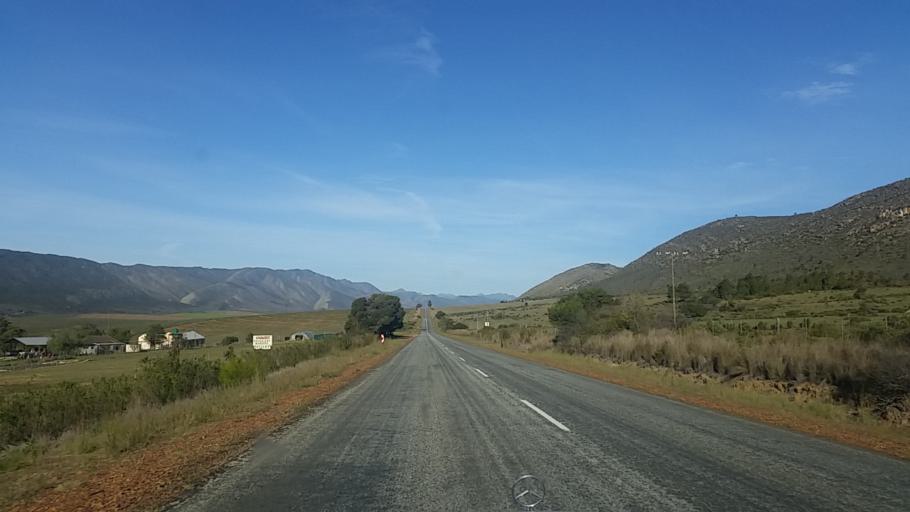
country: ZA
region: Western Cape
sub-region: Eden District Municipality
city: Knysna
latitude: -33.7727
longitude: 22.9266
